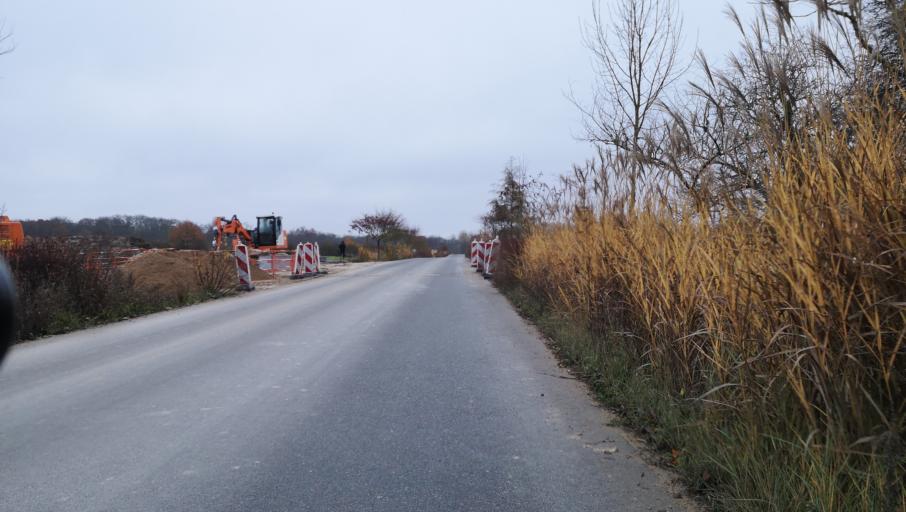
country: FR
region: Centre
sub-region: Departement du Loiret
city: Marigny-les-Usages
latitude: 47.9474
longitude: 2.0096
